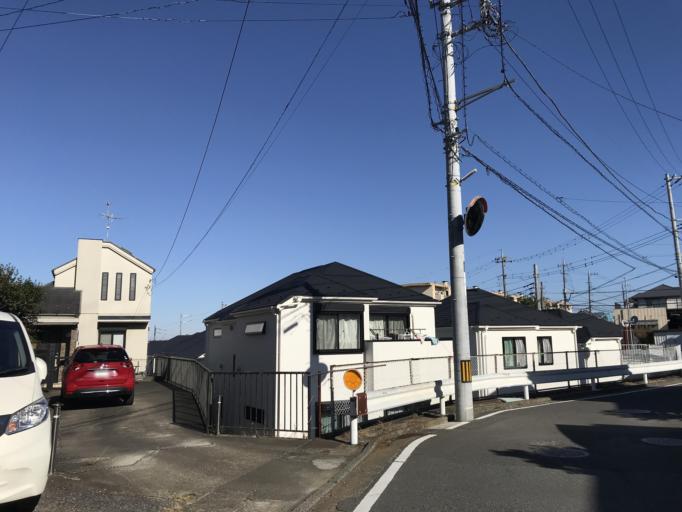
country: JP
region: Tokyo
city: Chofugaoka
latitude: 35.5685
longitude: 139.5861
